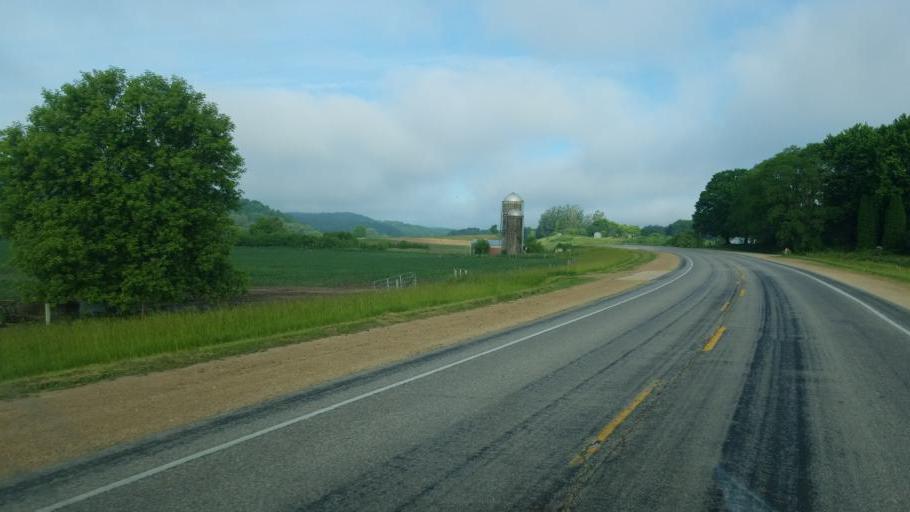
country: US
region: Wisconsin
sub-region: Vernon County
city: Hillsboro
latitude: 43.6598
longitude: -90.3751
